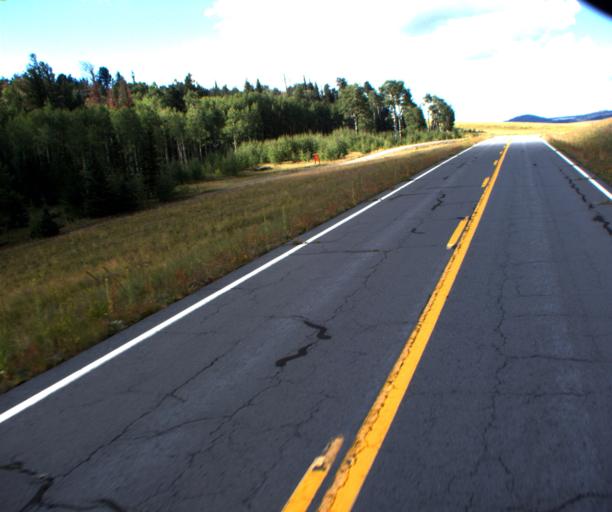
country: US
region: Arizona
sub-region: Apache County
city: Eagar
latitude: 33.9855
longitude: -109.3685
